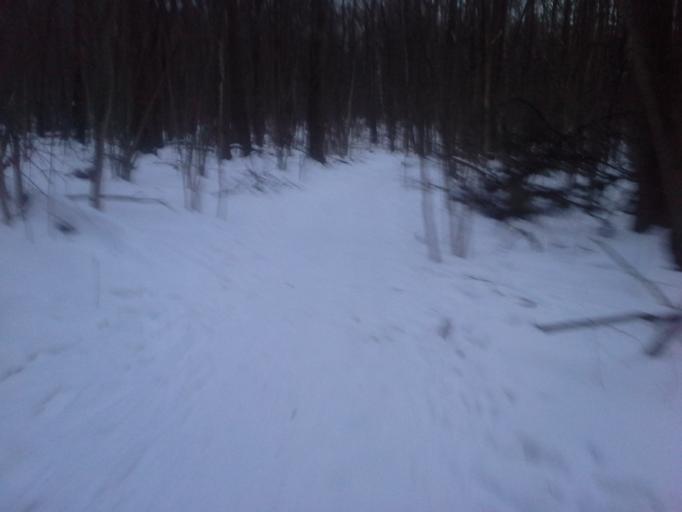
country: RU
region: Moscow
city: Yasenevo
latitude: 55.5641
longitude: 37.5389
